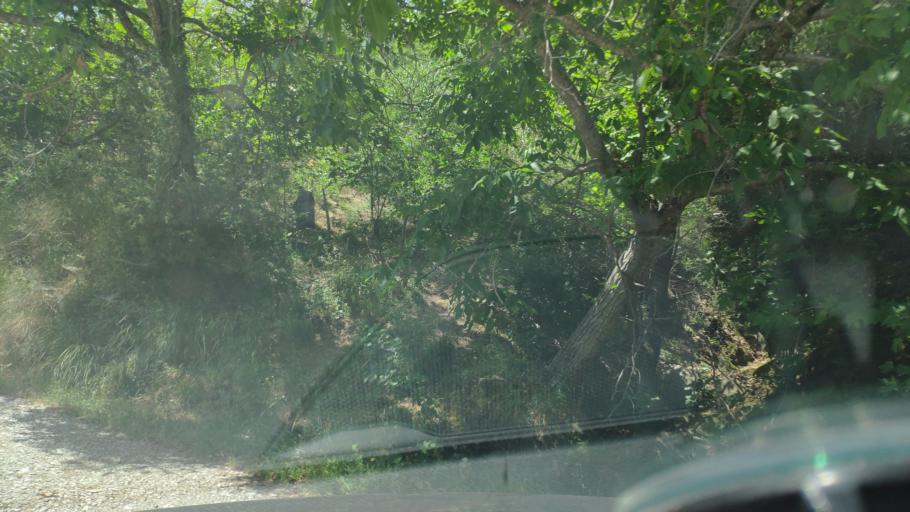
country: GR
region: Thessaly
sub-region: Nomos Kardhitsas
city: Anthiro
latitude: 39.2482
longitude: 21.3891
